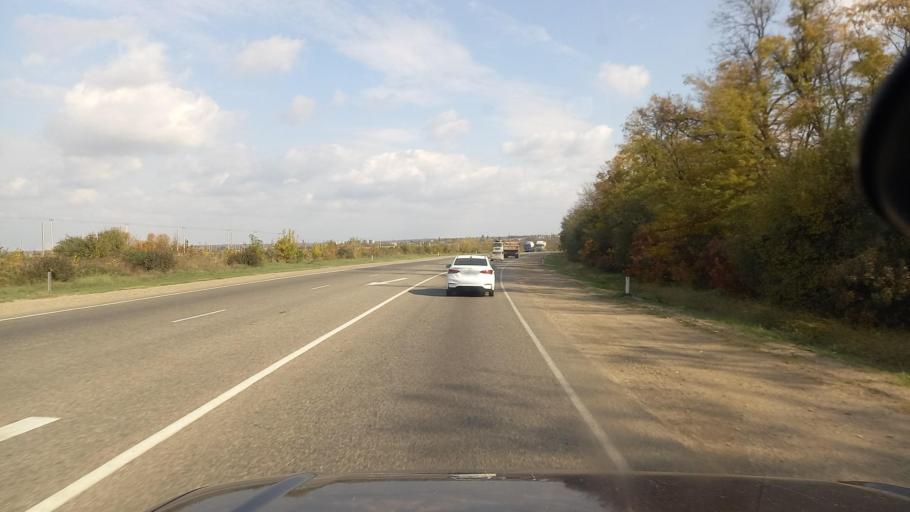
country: RU
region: Krasnodarskiy
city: Akhtyrskiy
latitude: 44.8504
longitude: 38.3169
